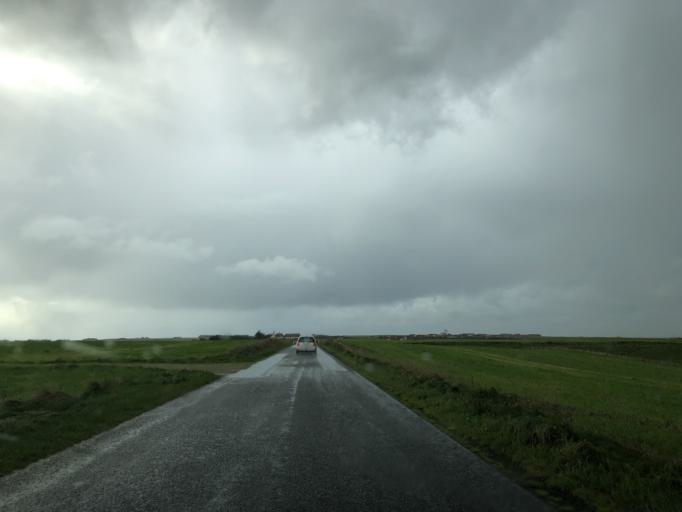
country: DK
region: Central Jutland
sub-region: Lemvig Kommune
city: Harboore
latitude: 56.5355
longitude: 8.1374
